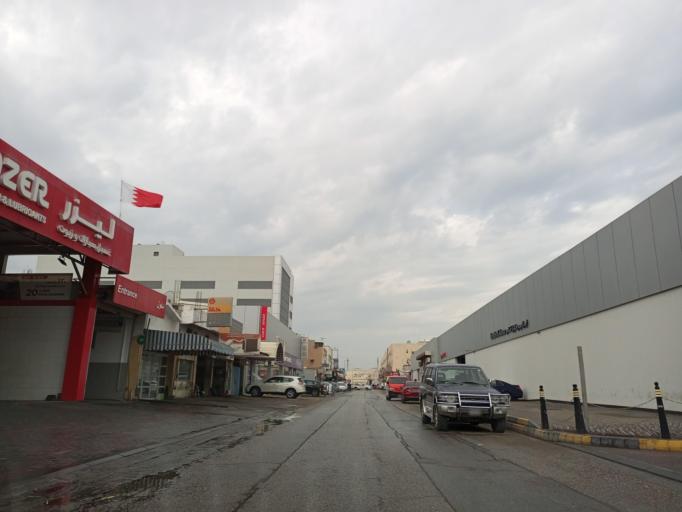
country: BH
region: Muharraq
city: Al Hadd
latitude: 26.2584
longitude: 50.6431
